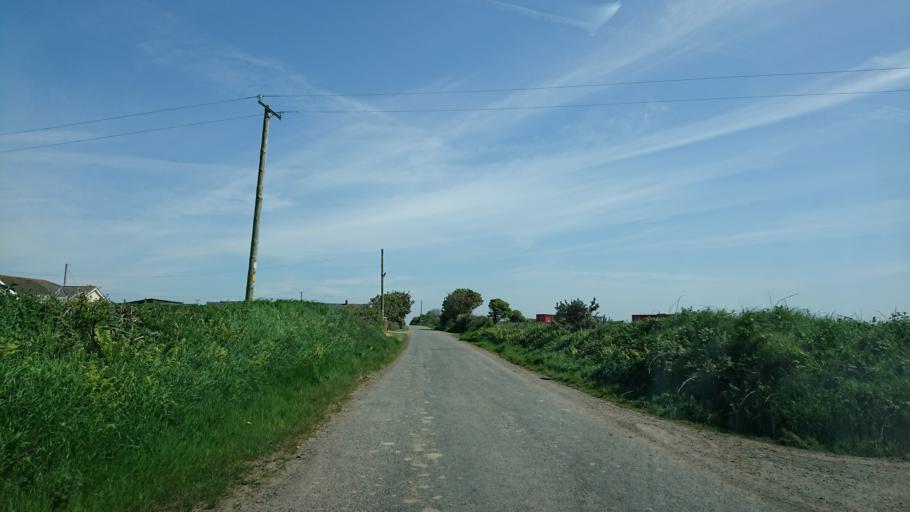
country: IE
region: Munster
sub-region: Waterford
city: Tra Mhor
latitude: 52.1445
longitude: -7.0834
